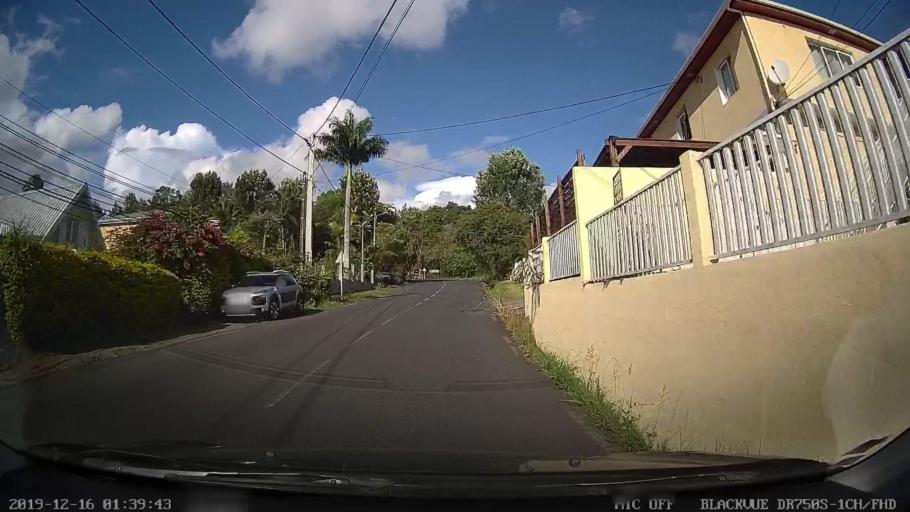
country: RE
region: Reunion
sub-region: Reunion
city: Le Tampon
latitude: -21.2615
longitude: 55.5083
